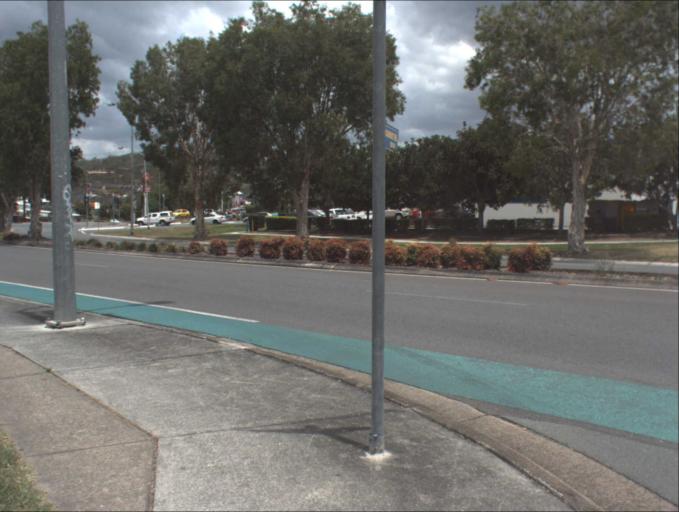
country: AU
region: Queensland
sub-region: Logan
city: Beenleigh
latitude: -27.7185
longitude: 153.2046
